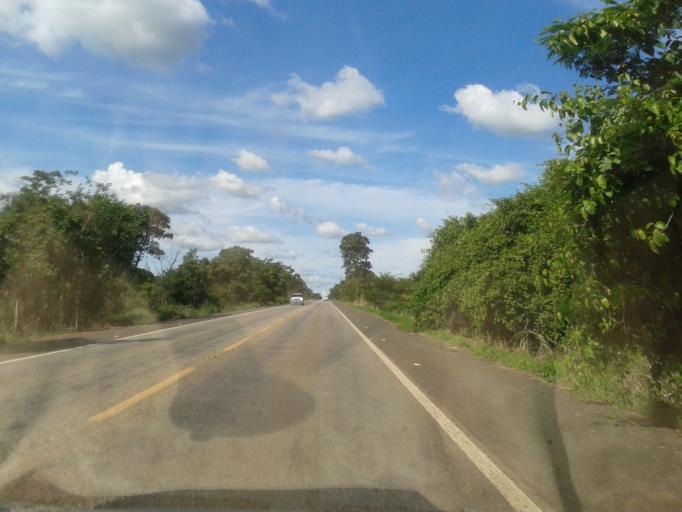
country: BR
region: Goias
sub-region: Mozarlandia
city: Mozarlandia
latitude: -15.0629
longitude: -50.6148
